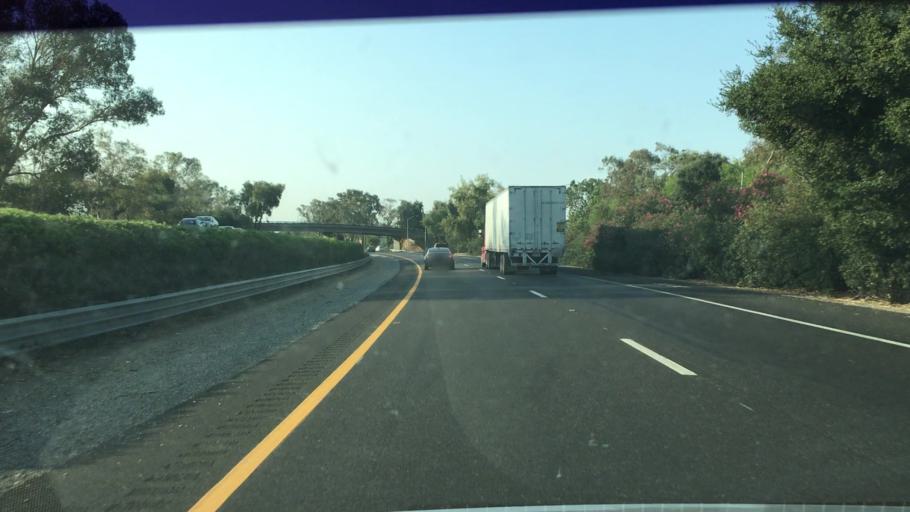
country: US
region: California
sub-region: San Joaquin County
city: Lodi
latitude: 38.1449
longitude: -121.2612
